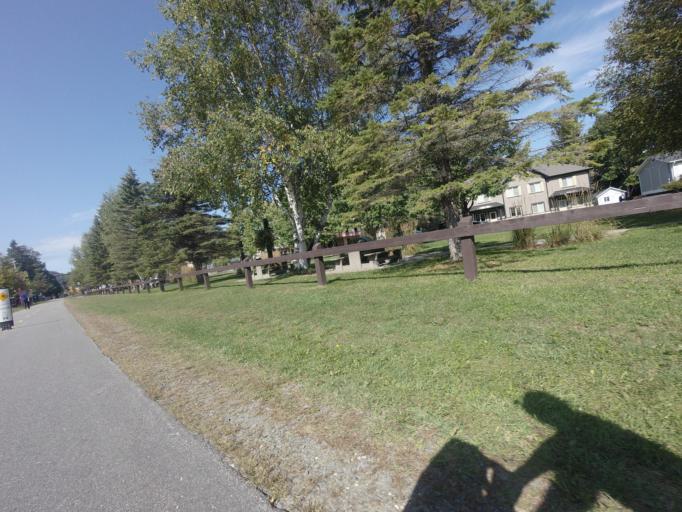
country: CA
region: Quebec
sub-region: Laurentides
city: Mont-Tremblant
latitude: 46.1297
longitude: -74.5895
